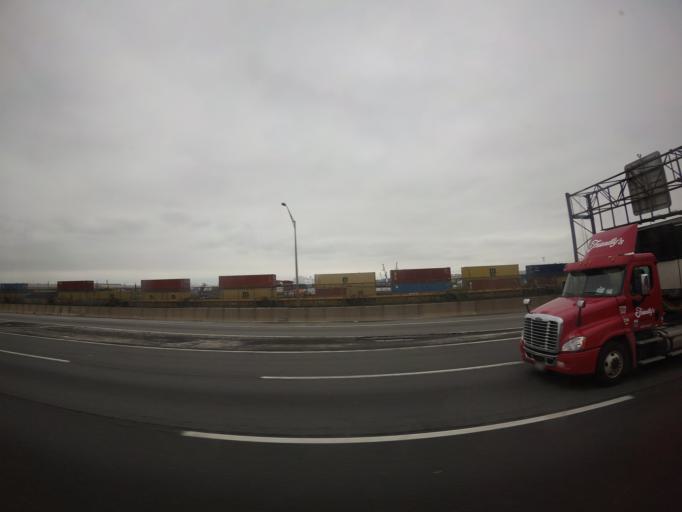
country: US
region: New Jersey
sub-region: Essex County
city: Newark
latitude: 40.6998
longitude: -74.1550
